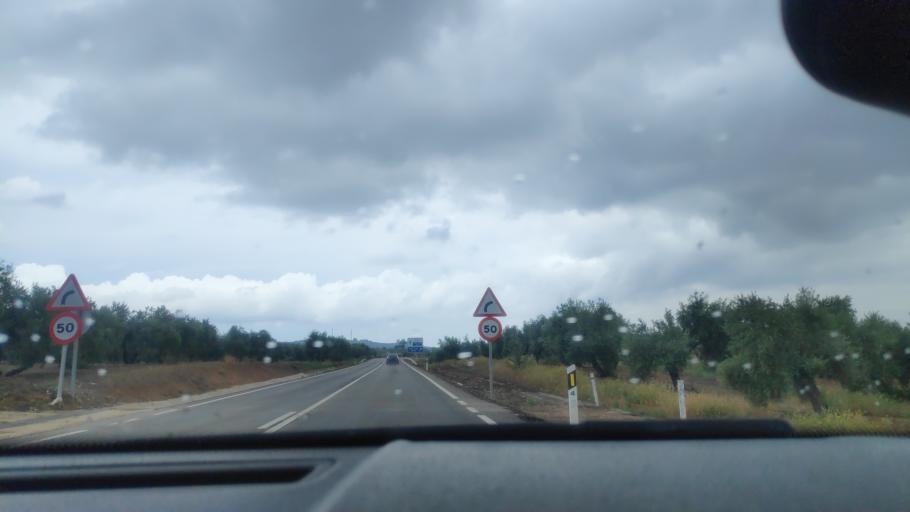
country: ES
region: Andalusia
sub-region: Provincia de Jaen
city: Jabalquinto
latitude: 38.0248
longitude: -3.7749
